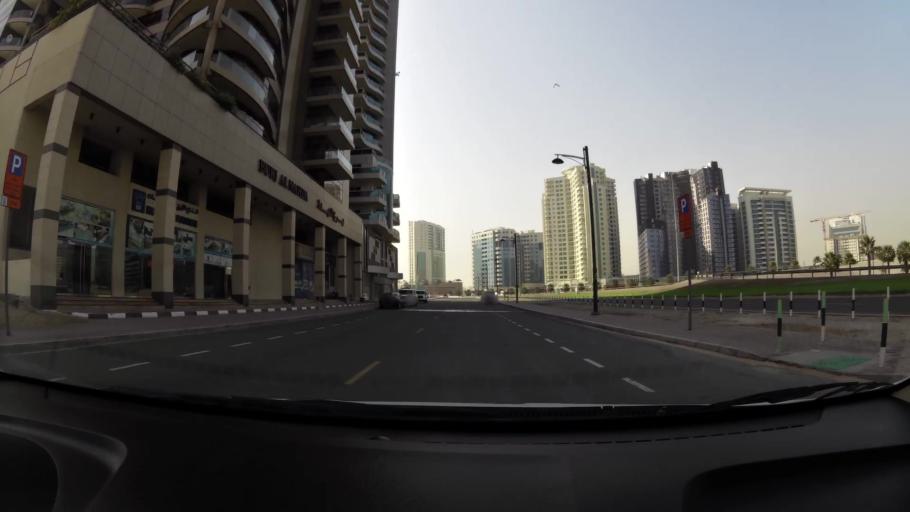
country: AE
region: Ash Shariqah
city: Sharjah
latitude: 25.2914
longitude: 55.3614
